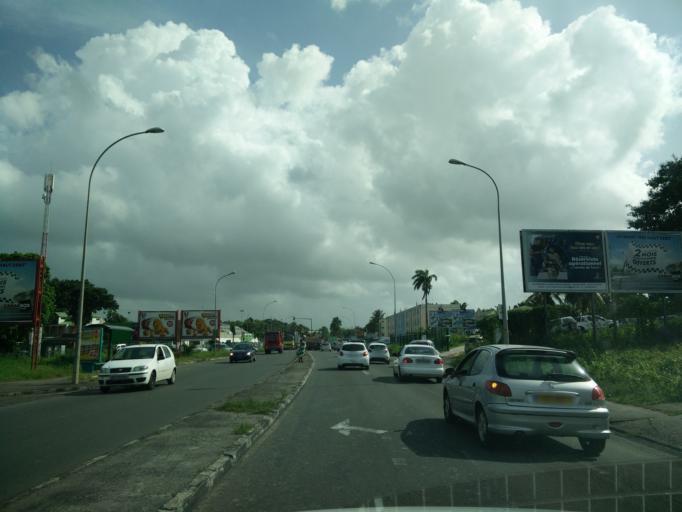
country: GP
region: Guadeloupe
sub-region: Guadeloupe
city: Pointe-a-Pitre
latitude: 16.2557
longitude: -61.5214
